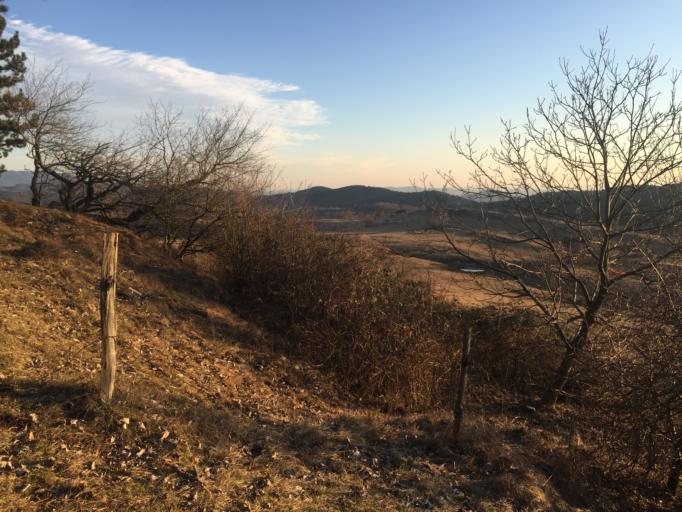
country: SI
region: Kanal
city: Kanal
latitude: 46.0456
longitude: 13.6898
